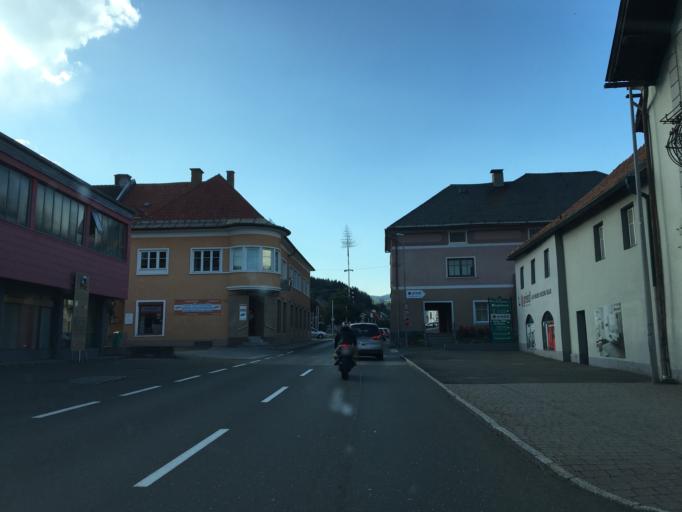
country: AT
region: Styria
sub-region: Politischer Bezirk Murau
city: Neumarkt in Steiermark
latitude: 47.0711
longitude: 14.4274
